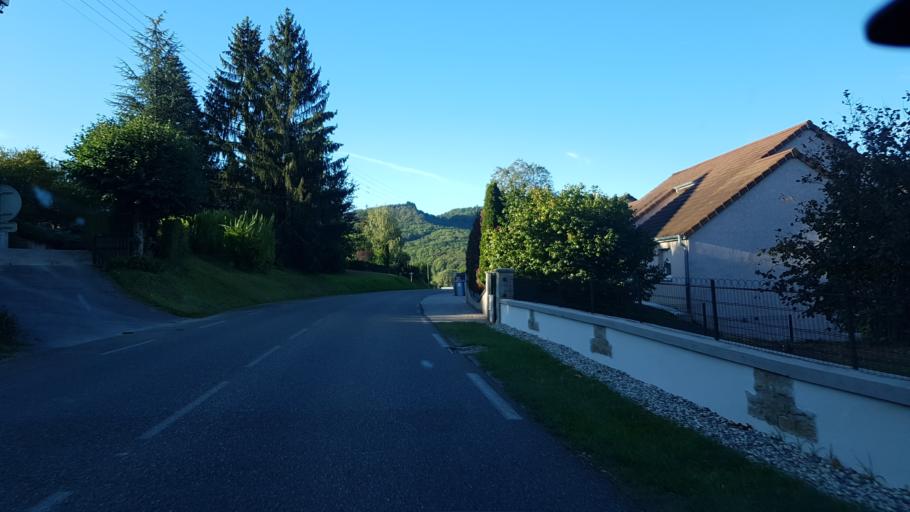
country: FR
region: Franche-Comte
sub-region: Departement du Jura
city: Lons-le-Saunier
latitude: 46.6564
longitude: 5.5394
